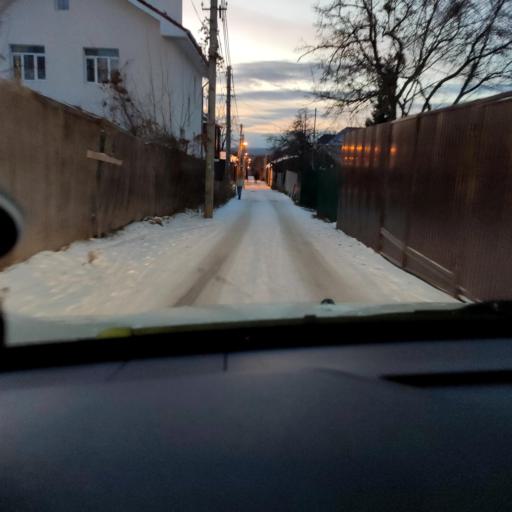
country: RU
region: Samara
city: Samara
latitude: 53.2590
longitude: 50.1968
